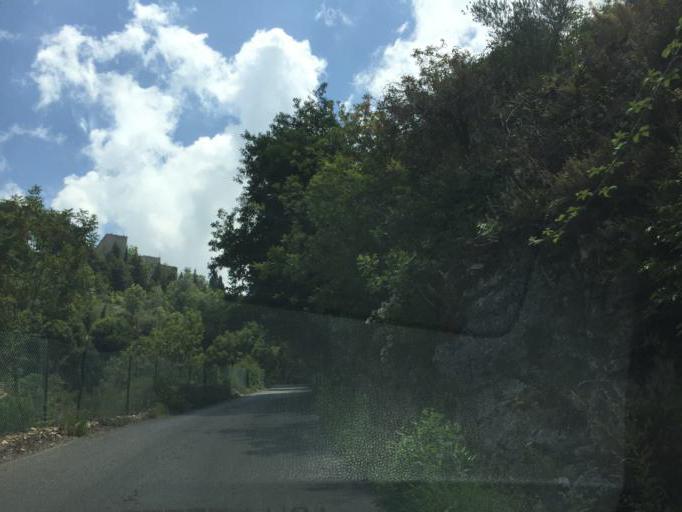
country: LB
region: Mont-Liban
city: Beit ed Dine
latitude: 33.6953
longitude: 35.5768
